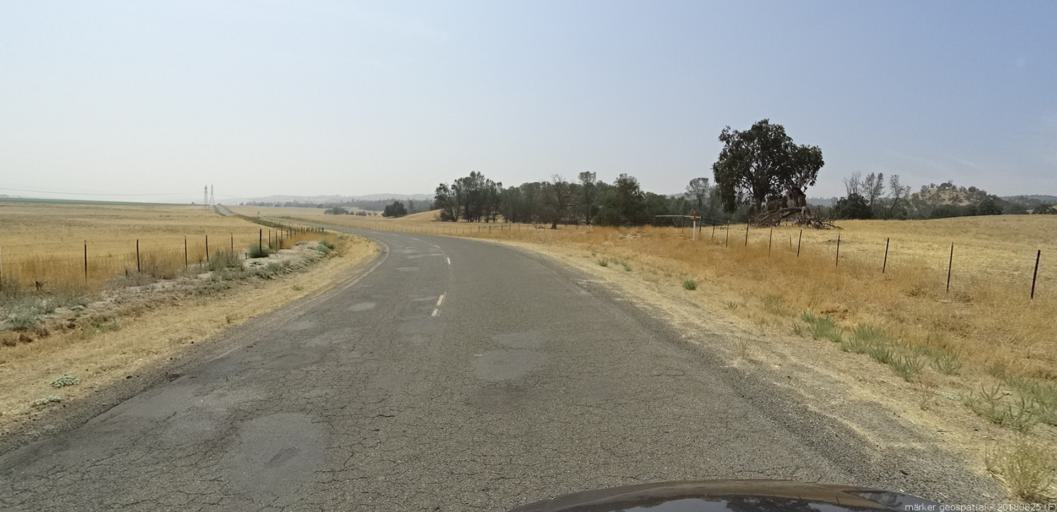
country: US
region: California
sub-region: San Luis Obispo County
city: Shandon
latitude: 35.8252
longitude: -120.3850
